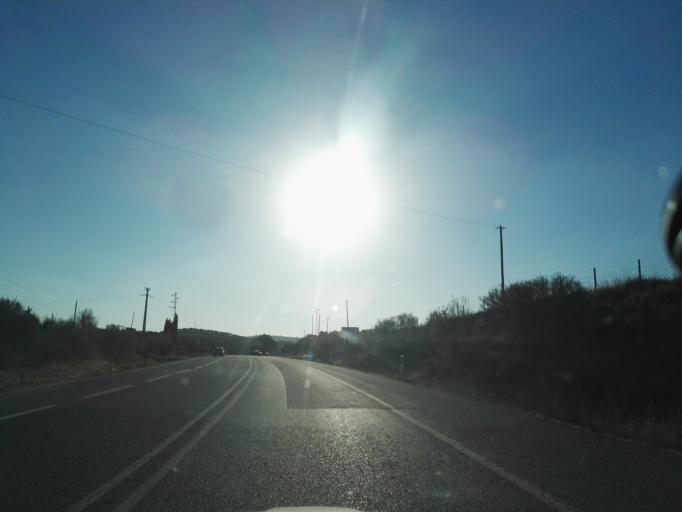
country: PT
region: Evora
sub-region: Borba
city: Borba
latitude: 38.8240
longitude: -7.4233
